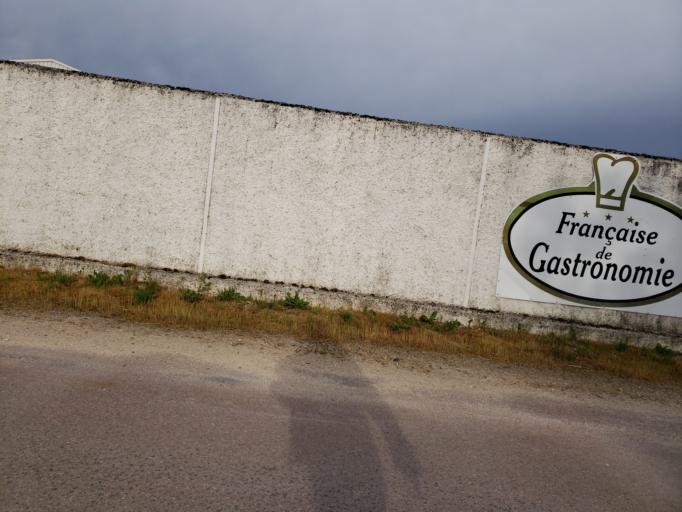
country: FR
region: Bourgogne
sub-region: Departement de l'Yonne
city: Cheny
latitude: 47.9269
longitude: 3.5151
